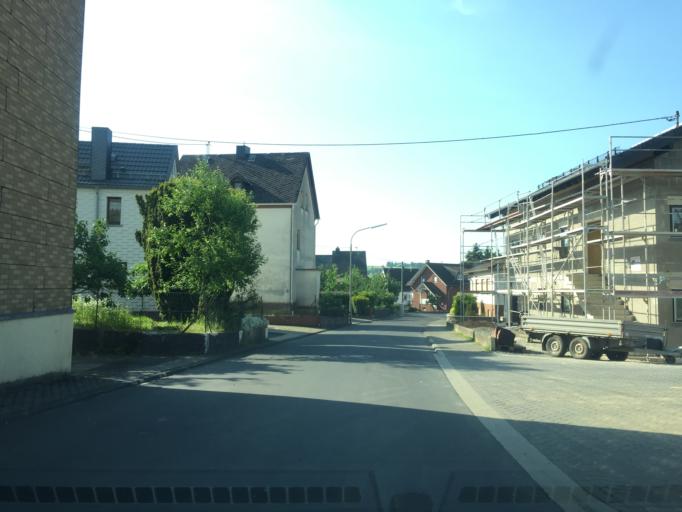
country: DE
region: Rheinland-Pfalz
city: Girod
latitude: 50.4458
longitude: 7.9063
